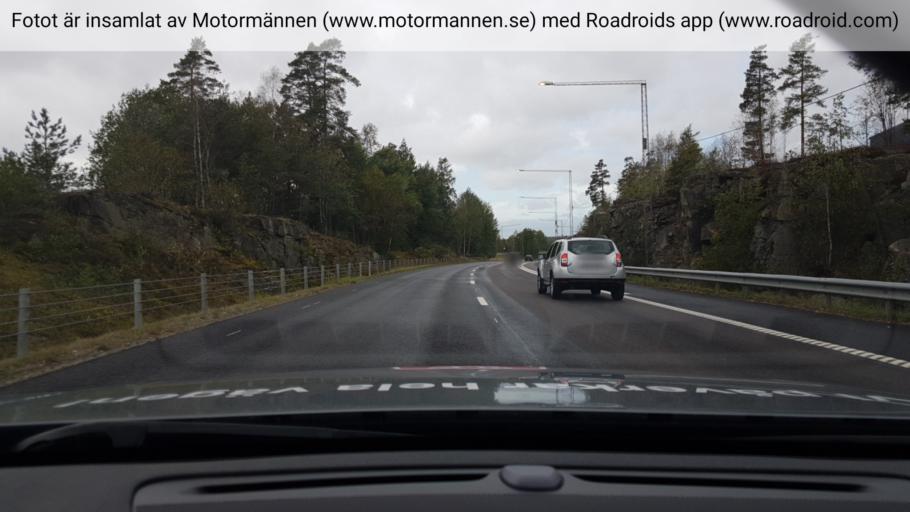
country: SE
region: Vaermland
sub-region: Hammaro Kommun
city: Skoghall
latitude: 59.3786
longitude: 13.4363
